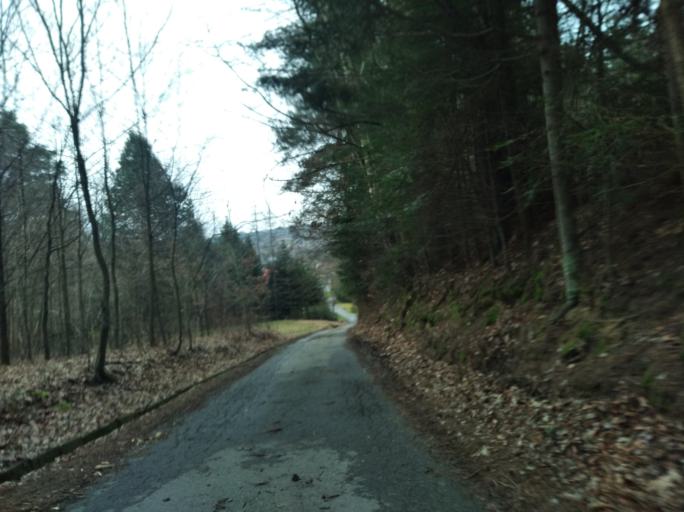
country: PL
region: Subcarpathian Voivodeship
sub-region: Powiat strzyzowski
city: Strzyzow
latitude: 49.9004
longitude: 21.8194
